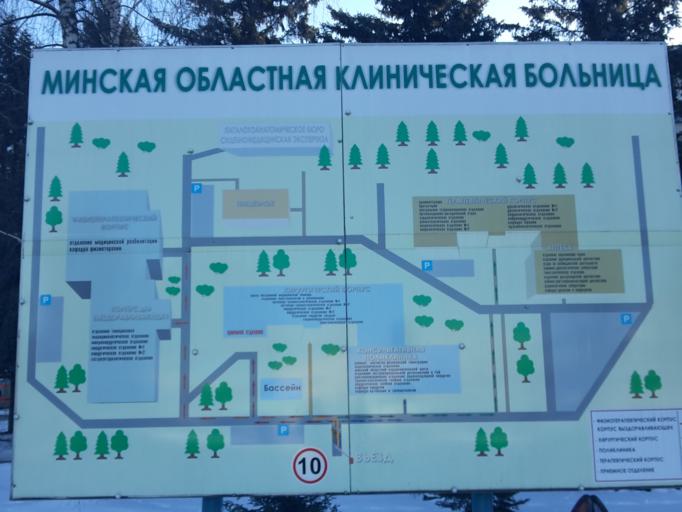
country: BY
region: Minsk
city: Lyasny
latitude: 54.0045
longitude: 27.6867
